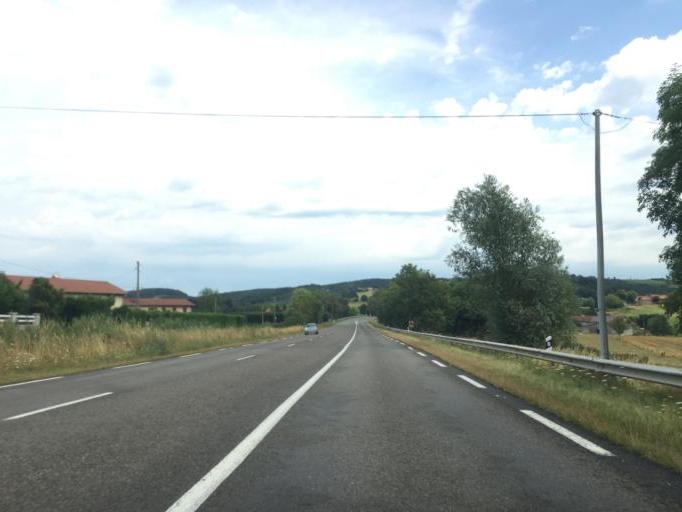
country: FR
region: Rhone-Alpes
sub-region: Departement de la Loire
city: Saint-Symphorien-de-Lay
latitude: 45.9423
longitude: 4.2601
